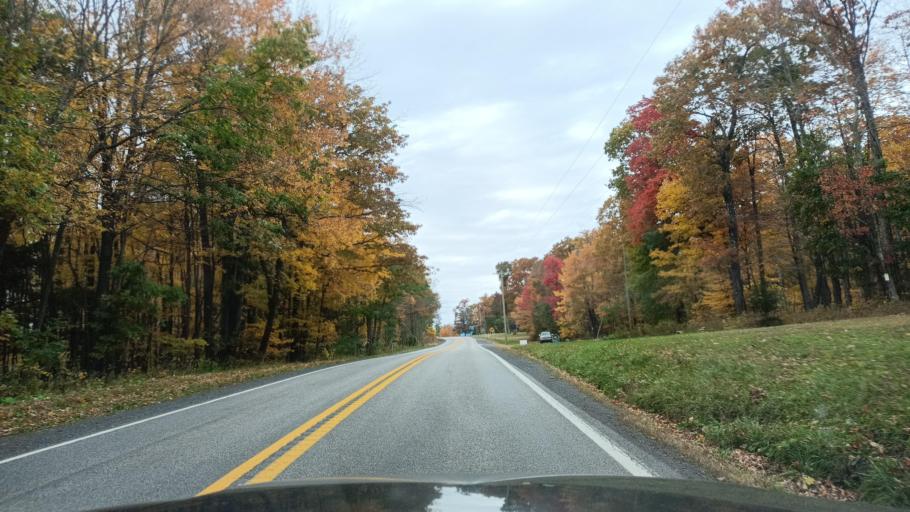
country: US
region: Maryland
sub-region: Garrett County
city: Mountain Lake Park
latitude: 39.2464
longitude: -79.2255
